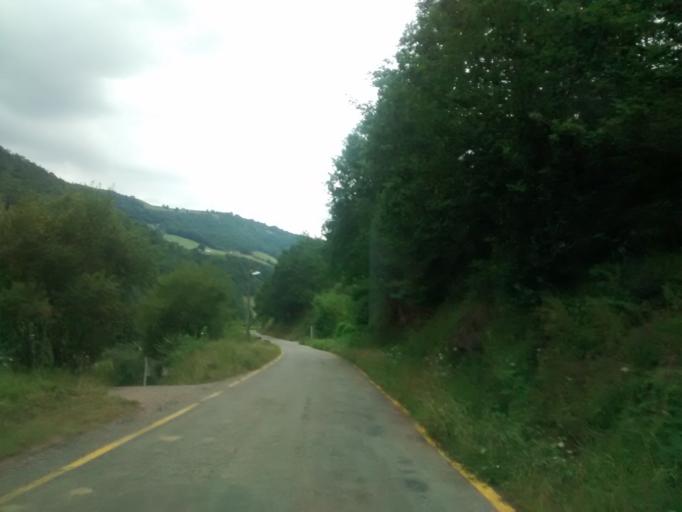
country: ES
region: Cantabria
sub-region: Provincia de Cantabria
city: Vega de Pas
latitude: 43.1420
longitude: -3.7657
